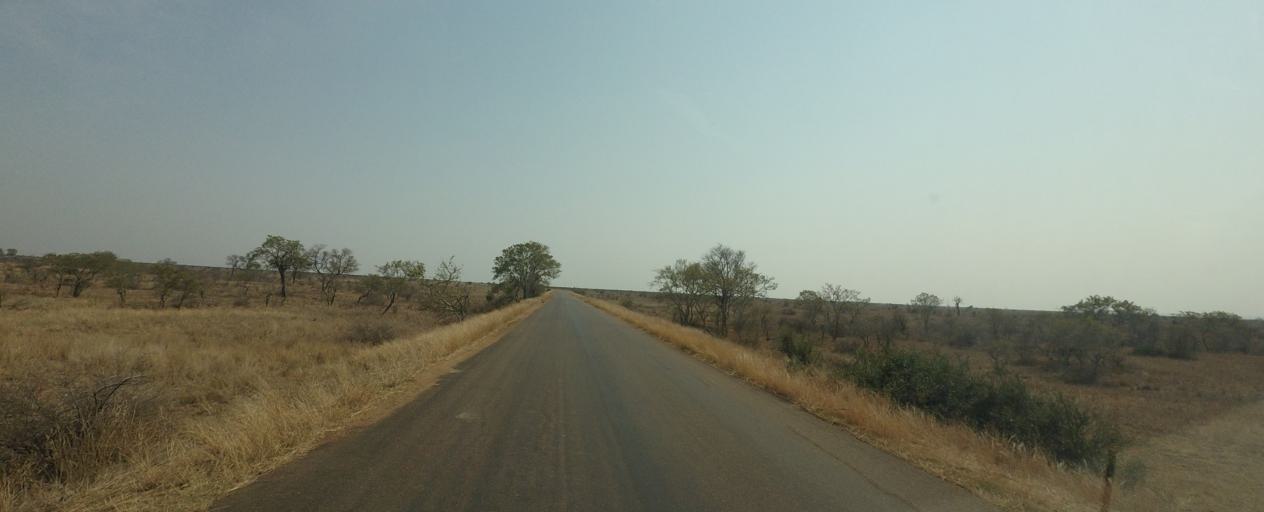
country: ZA
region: Limpopo
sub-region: Mopani District Municipality
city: Phalaborwa
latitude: -24.2667
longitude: 31.7302
